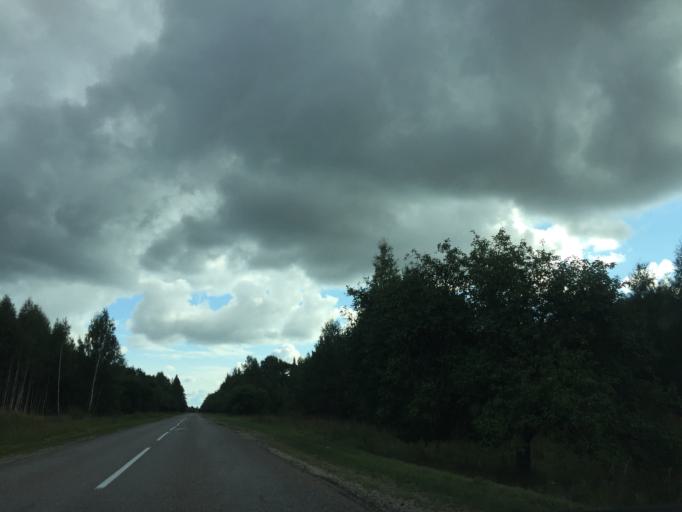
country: LV
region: Limbazu Rajons
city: Limbazi
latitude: 57.3647
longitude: 24.6715
